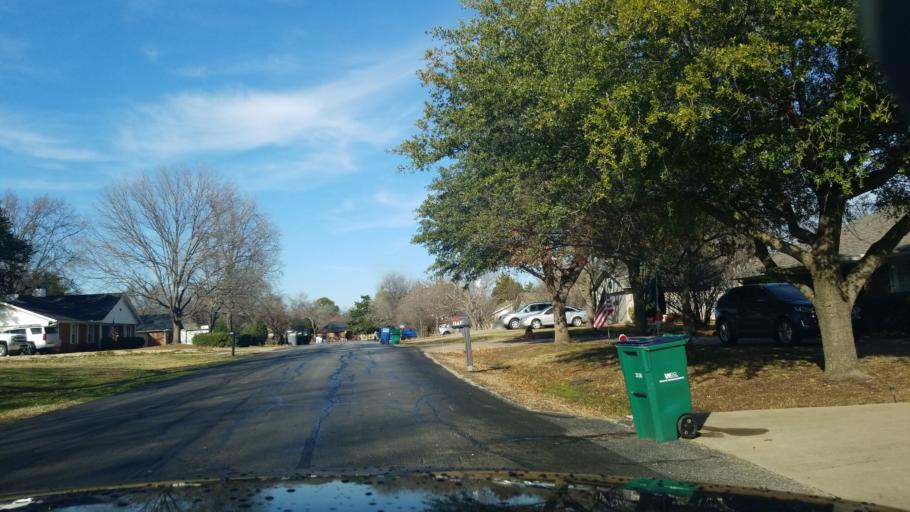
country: US
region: Texas
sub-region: Denton County
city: Corinth
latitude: 33.1510
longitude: -97.0643
